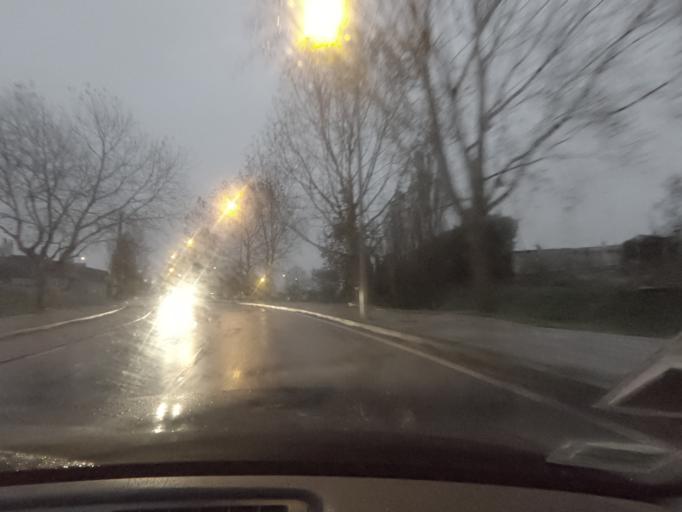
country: PT
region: Porto
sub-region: Matosinhos
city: Matosinhos
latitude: 41.1880
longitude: -8.6770
